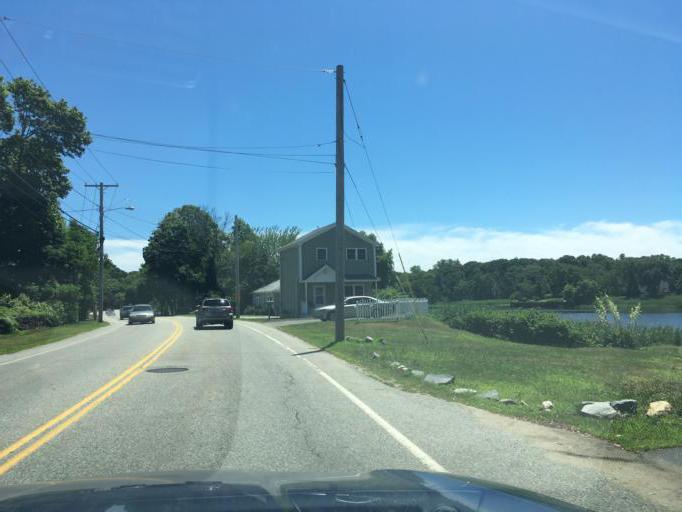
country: US
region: Rhode Island
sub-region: Kent County
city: Warwick
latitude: 41.7002
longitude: -71.3832
